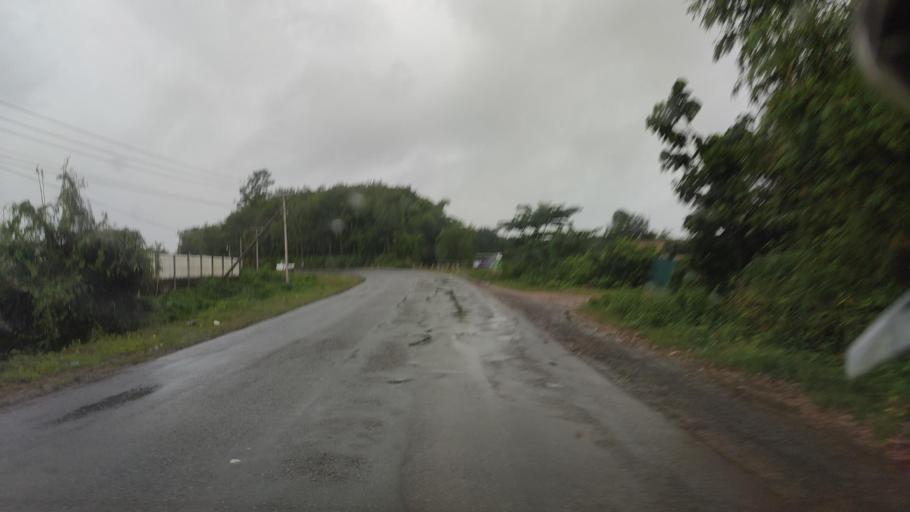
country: MM
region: Bago
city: Bago
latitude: 17.3598
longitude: 96.4527
